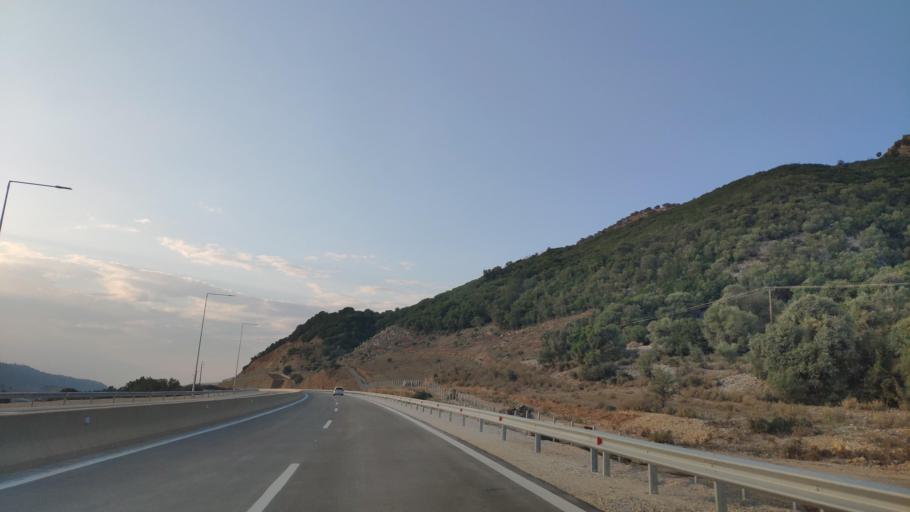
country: GR
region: West Greece
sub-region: Nomos Aitolias kai Akarnanias
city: Katouna
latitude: 38.7901
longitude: 21.1421
